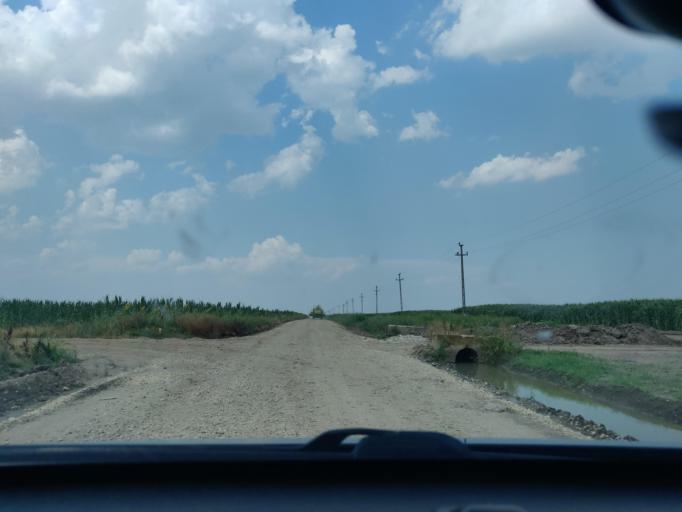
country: RO
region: Teleorman
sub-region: Comuna Sarbeni
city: Sarbeni
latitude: 44.4849
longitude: 25.3900
